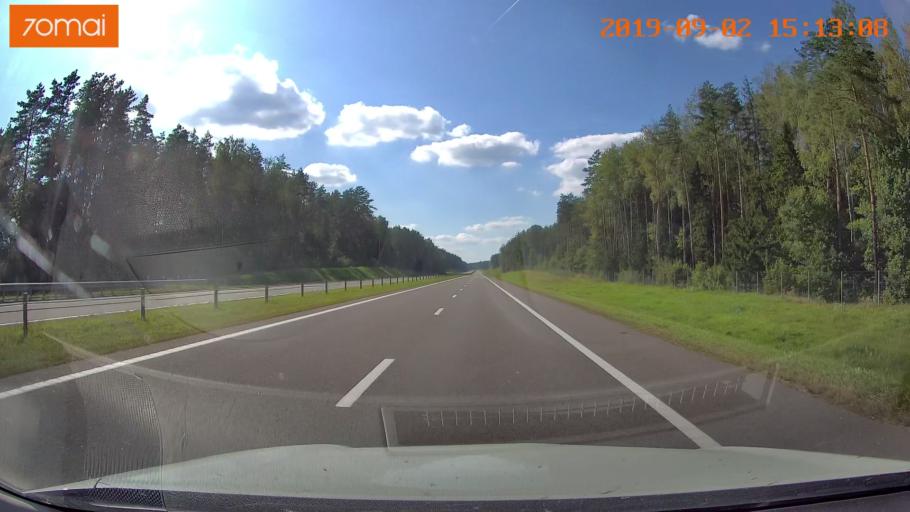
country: BY
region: Mogilev
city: Byalynichy
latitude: 53.9659
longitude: 29.7093
